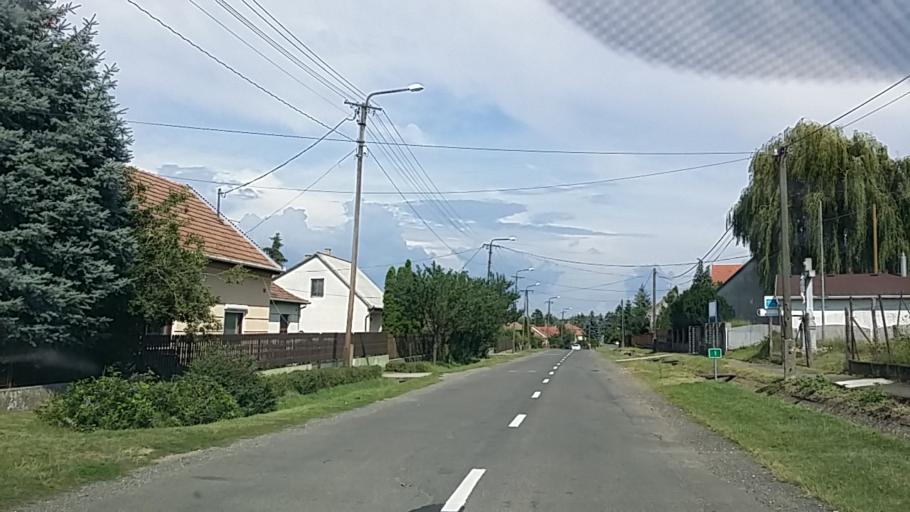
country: HU
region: Nograd
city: Nagyoroszi
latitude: 48.0525
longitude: 19.0419
